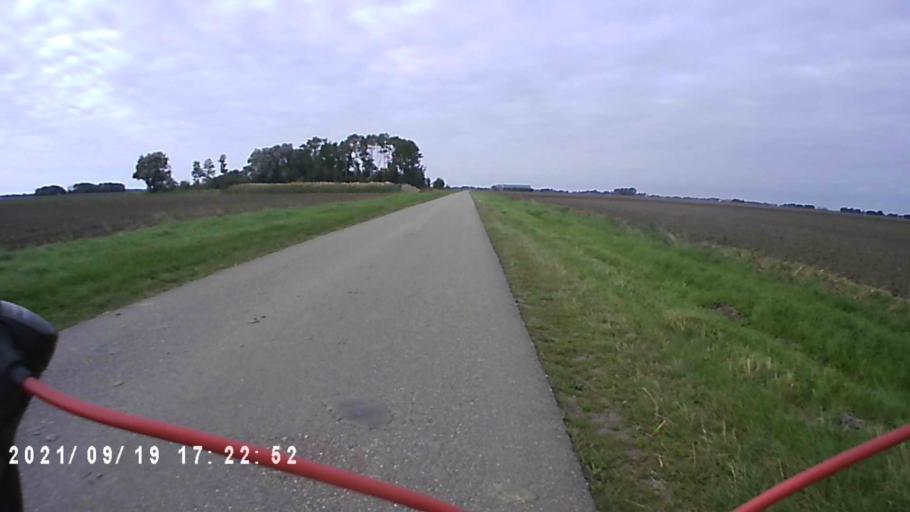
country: NL
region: Groningen
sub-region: Gemeente  Oldambt
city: Winschoten
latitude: 53.2121
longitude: 7.0180
